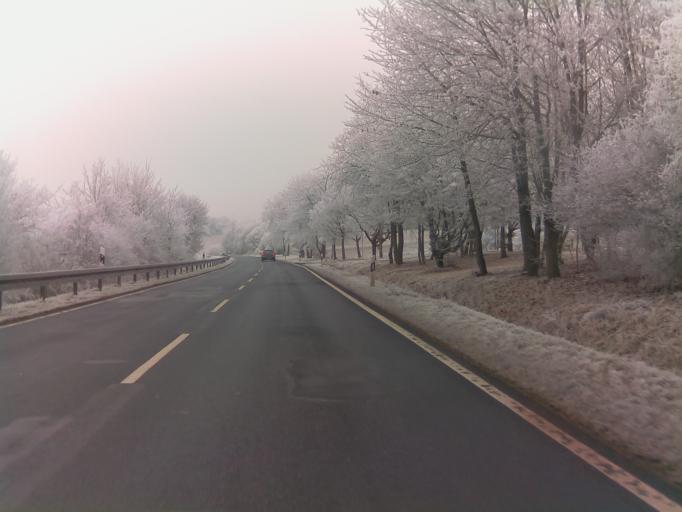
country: DE
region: Bavaria
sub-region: Regierungsbezirk Unterfranken
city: Sondheim vor der Rhoen
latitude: 50.4616
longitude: 10.1545
